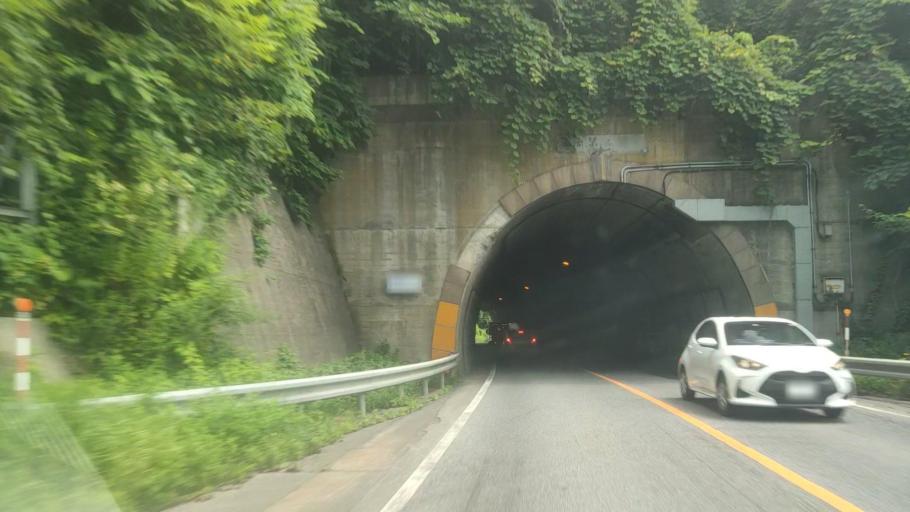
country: JP
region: Hokkaido
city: Niseko Town
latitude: 42.5889
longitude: 140.6778
